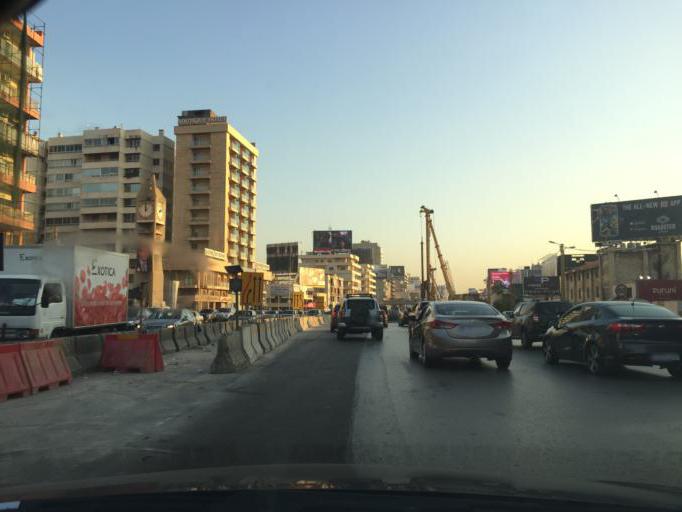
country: LB
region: Mont-Liban
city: Jdaidet el Matn
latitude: 33.9111
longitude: 35.5802
